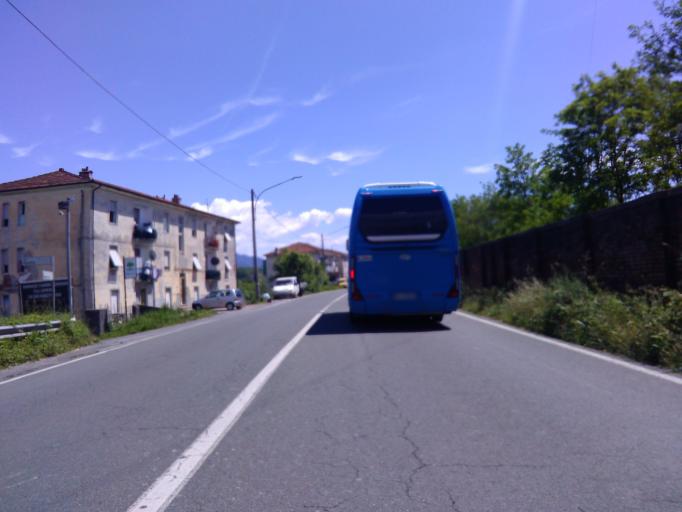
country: IT
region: Tuscany
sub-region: Provincia di Massa-Carrara
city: Terrarossa
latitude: 44.2254
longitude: 9.9684
